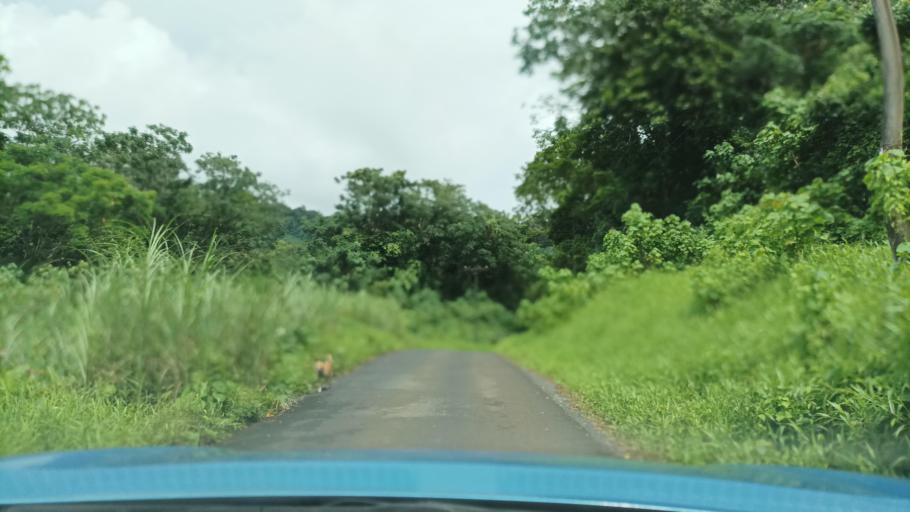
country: FM
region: Pohnpei
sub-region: Madolenihm Municipality
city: Madolenihm Municipality Government
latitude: 6.8964
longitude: 158.3166
